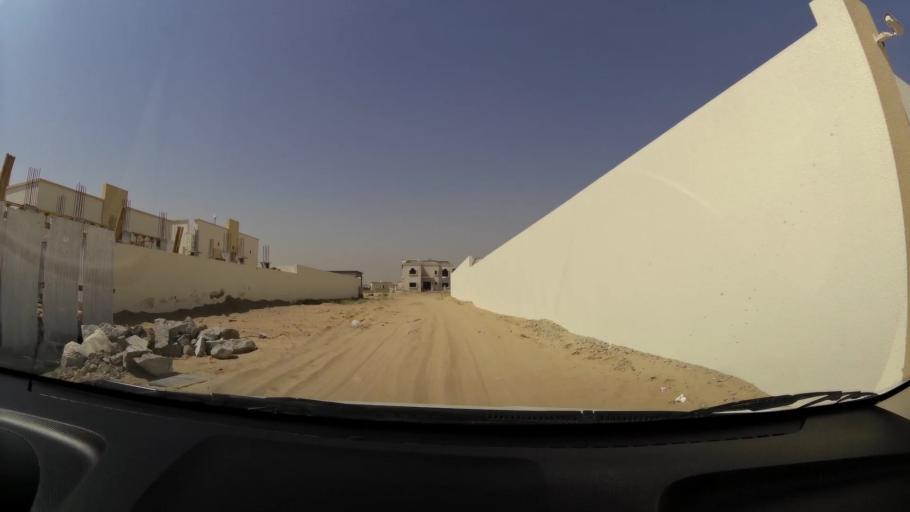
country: AE
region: Ajman
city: Ajman
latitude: 25.4001
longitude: 55.5443
